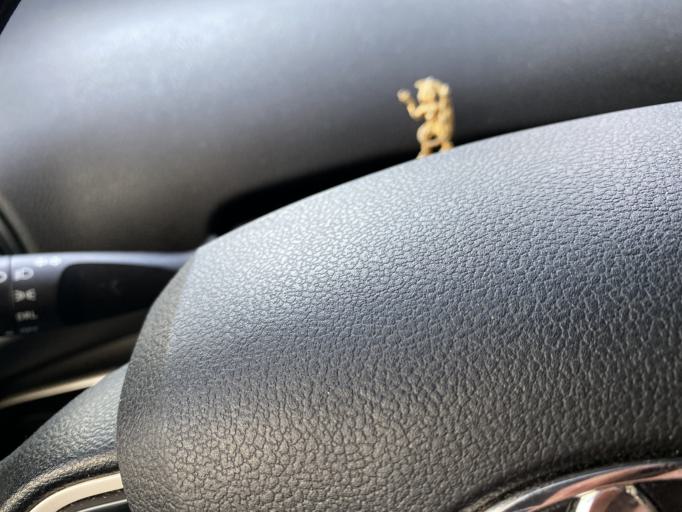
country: US
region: California
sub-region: Santa Clara County
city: Seven Trees
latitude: 37.2803
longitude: -121.8557
